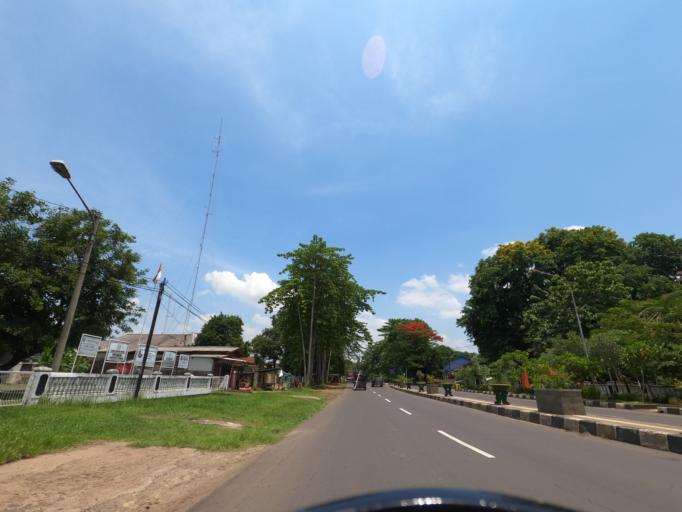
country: ID
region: West Java
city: Pamanukan
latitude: -6.5525
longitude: 107.7640
